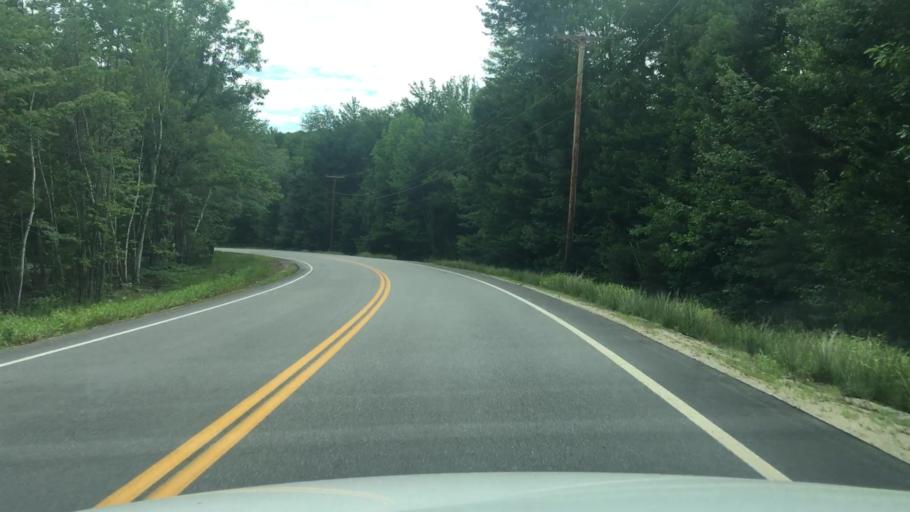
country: US
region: Maine
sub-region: Oxford County
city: West Paris
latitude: 44.3726
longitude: -70.4749
